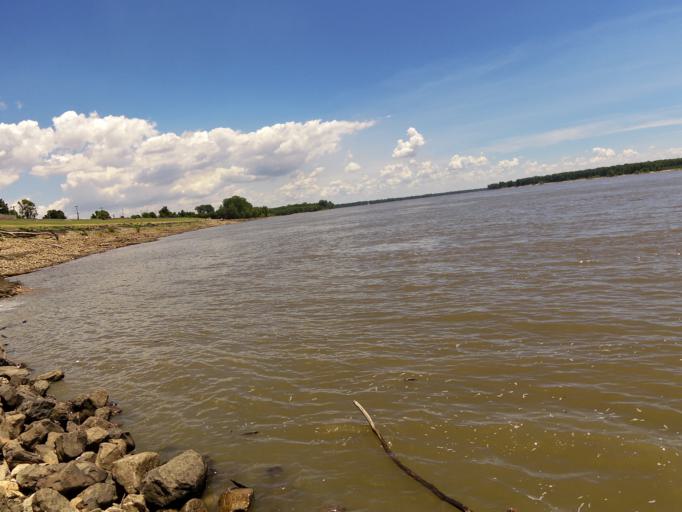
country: US
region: Missouri
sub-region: New Madrid County
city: New Madrid
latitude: 36.5828
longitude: -89.5333
